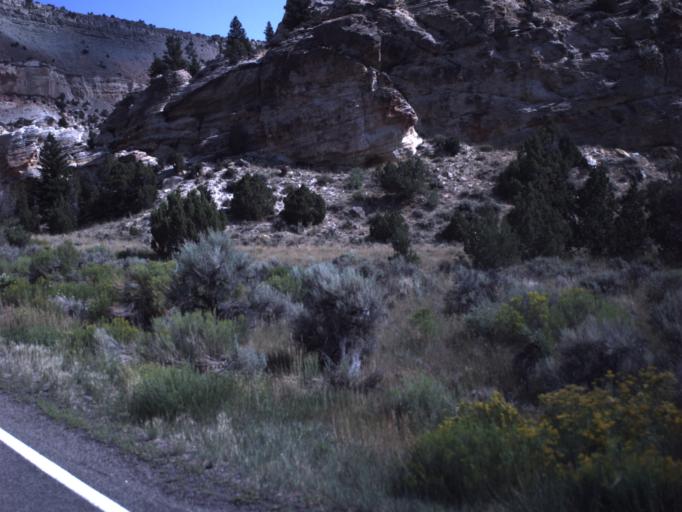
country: US
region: Utah
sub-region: Daggett County
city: Manila
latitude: 40.9286
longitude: -109.7213
